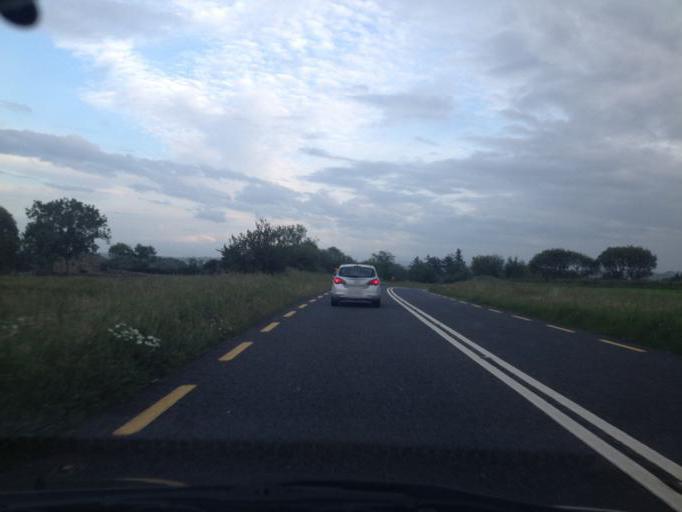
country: IE
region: Connaught
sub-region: Sligo
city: Sligo
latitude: 54.3490
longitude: -8.5048
